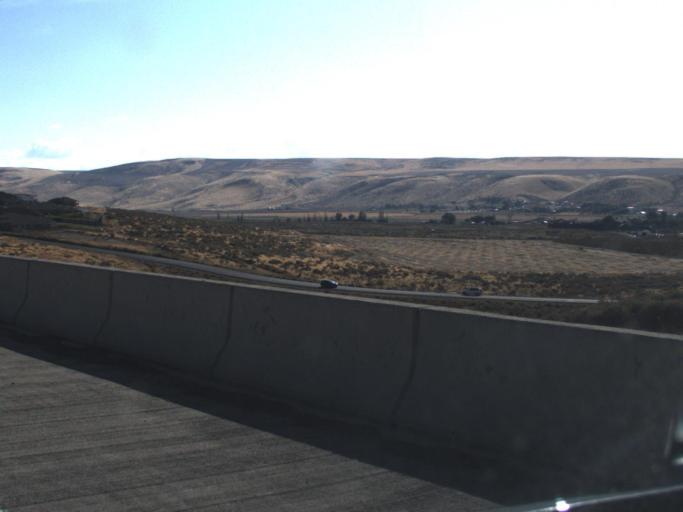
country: US
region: Washington
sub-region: Benton County
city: West Richland
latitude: 46.2169
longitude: -119.3478
